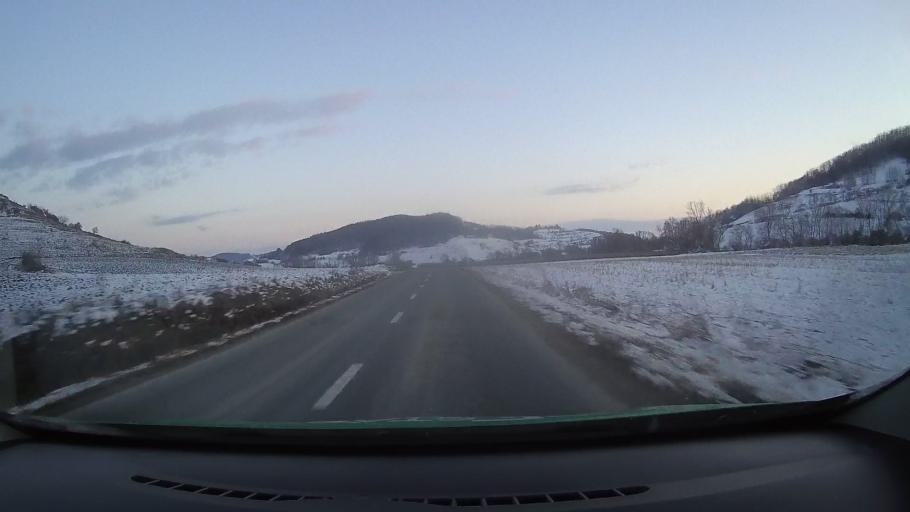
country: RO
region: Sibiu
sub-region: Comuna Alma
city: Alma
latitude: 46.1998
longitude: 24.4690
